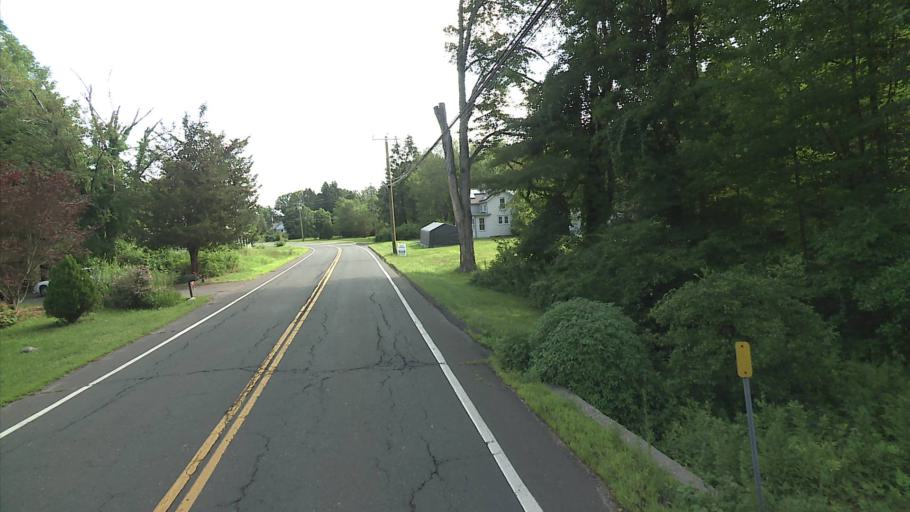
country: US
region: Connecticut
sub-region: Middlesex County
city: Moodus
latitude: 41.5088
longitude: -72.4386
